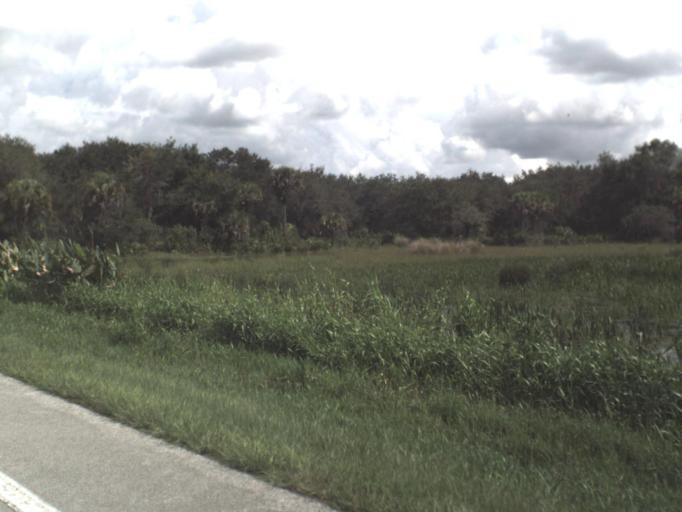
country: US
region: Florida
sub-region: Sarasota County
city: Warm Mineral Springs
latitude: 27.1935
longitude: -82.1773
